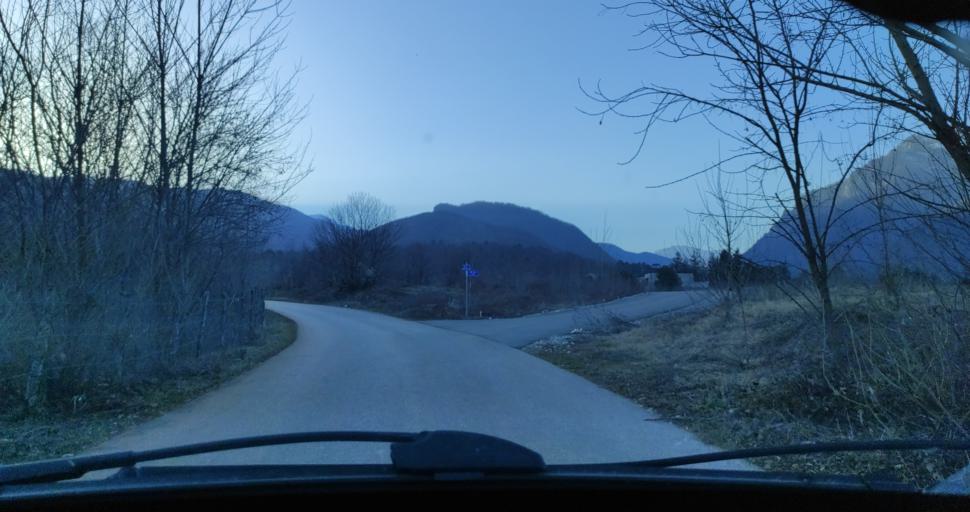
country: XK
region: Gjakova
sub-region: Komuna e Decanit
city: Decan
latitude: 42.5396
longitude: 20.2774
